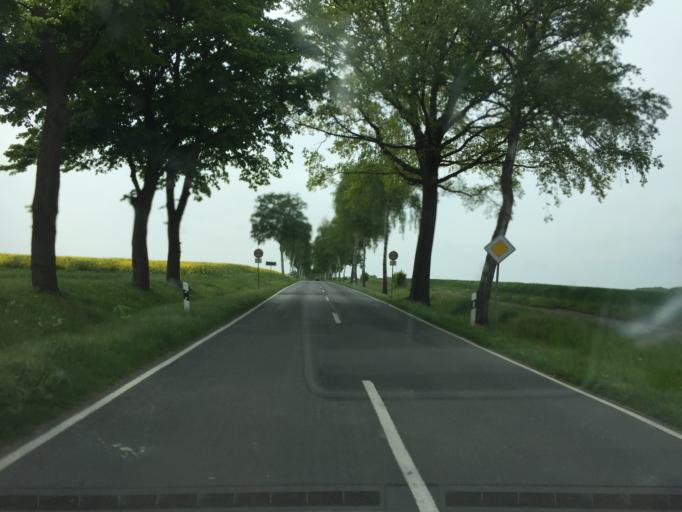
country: DE
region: Lower Saxony
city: Bassum
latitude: 52.8742
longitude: 8.7690
